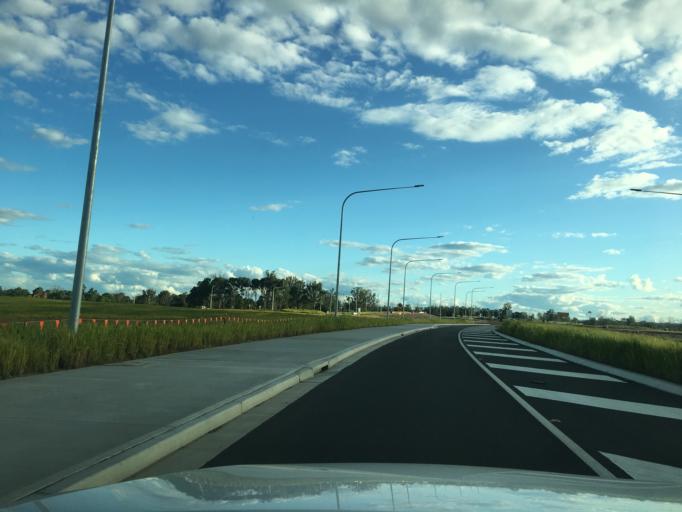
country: AU
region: New South Wales
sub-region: Liverpool
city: Bringelly
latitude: -33.8812
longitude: 150.7449
